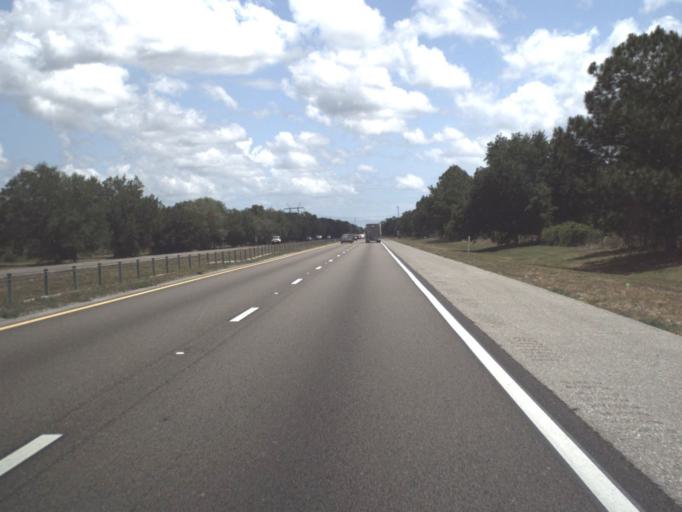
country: US
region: Florida
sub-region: Orange County
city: Wedgefield
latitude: 28.4523
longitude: -81.0217
